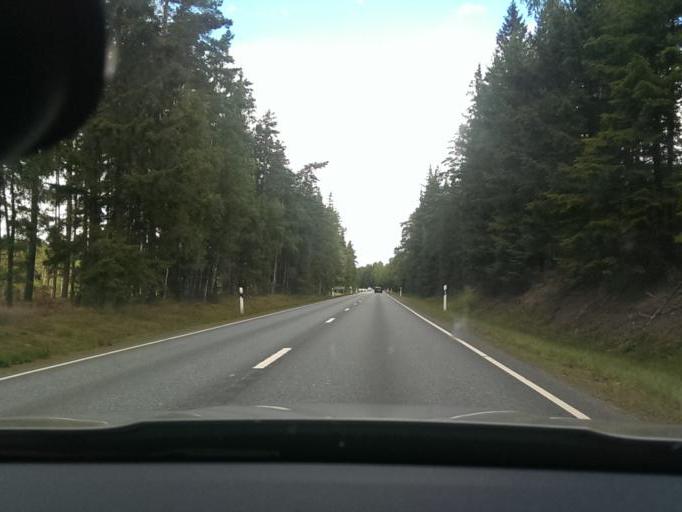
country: SE
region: Joenkoeping
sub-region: Varnamo Kommun
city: Varnamo
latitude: 57.2522
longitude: 13.9869
